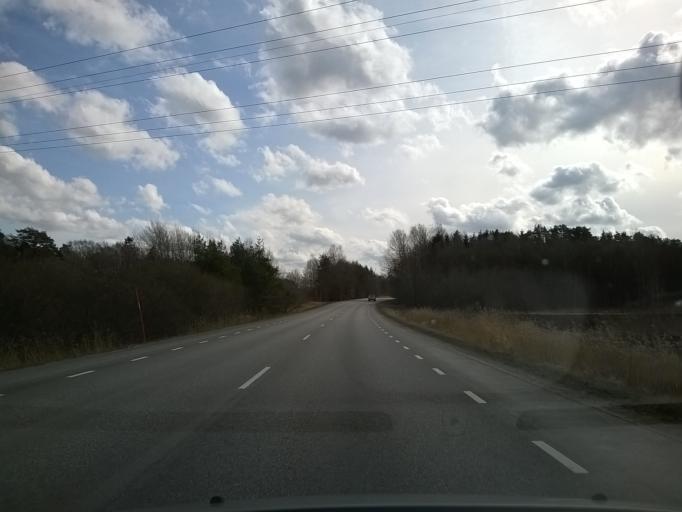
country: SE
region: Vaestra Goetaland
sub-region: Kungalvs Kommun
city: Kode
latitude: 57.9506
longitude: 11.8510
